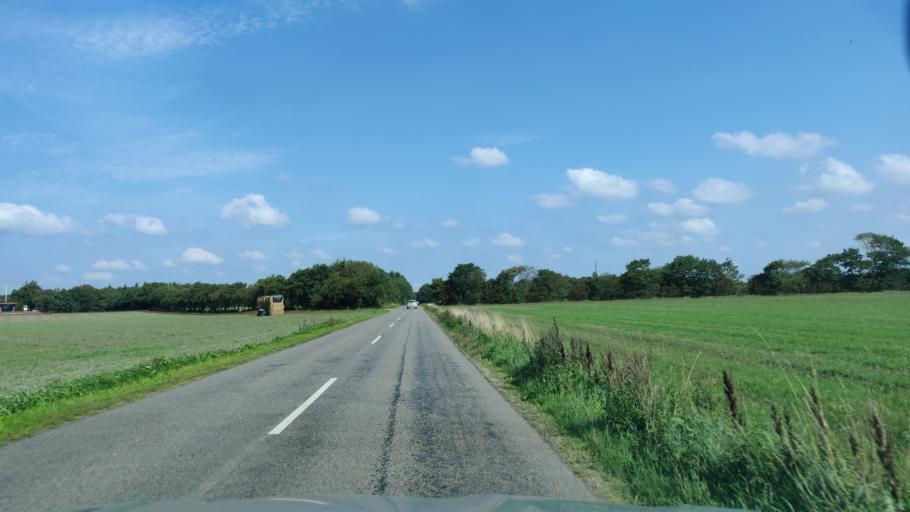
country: DK
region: Central Jutland
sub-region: Herning Kommune
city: Avlum
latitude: 56.2268
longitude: 8.8631
